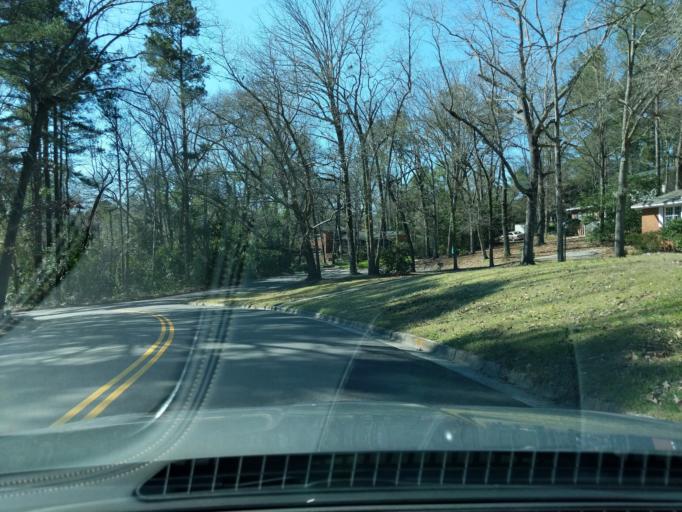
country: US
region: South Carolina
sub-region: Aiken County
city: Aiken
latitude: 33.5347
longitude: -81.7406
